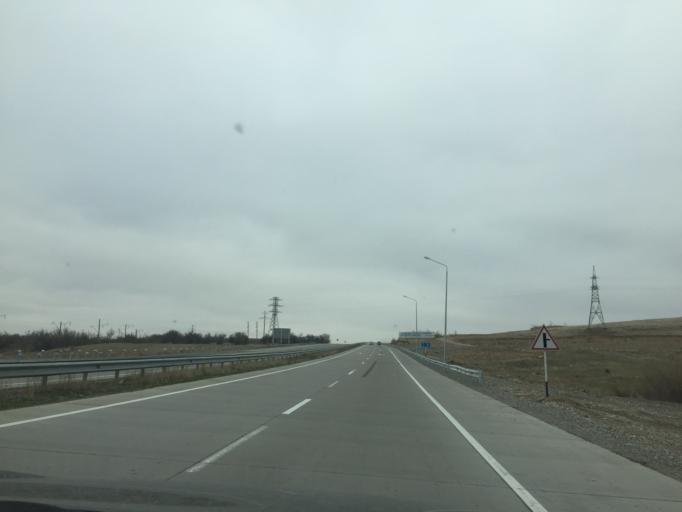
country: KZ
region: Ongtustik Qazaqstan
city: Sastobe
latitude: 42.5318
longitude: 70.0212
